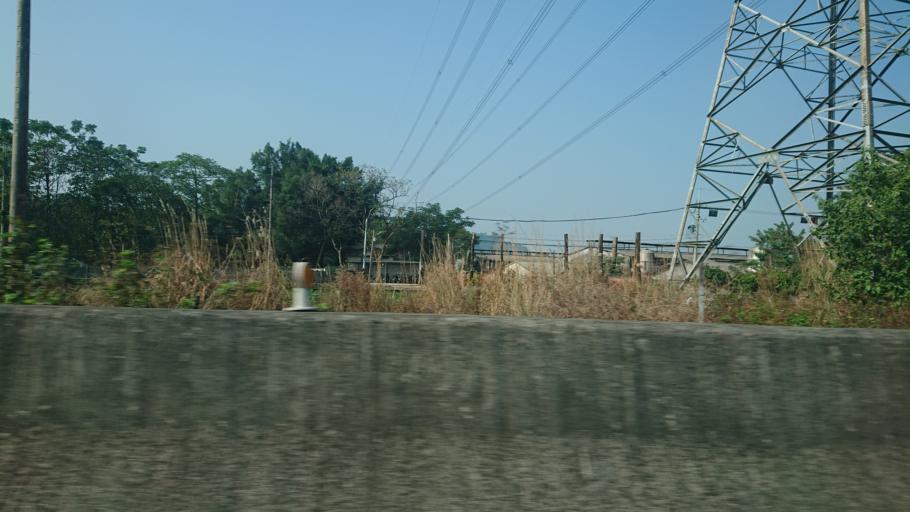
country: TW
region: Taiwan
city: Lugu
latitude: 23.7709
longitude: 120.6592
